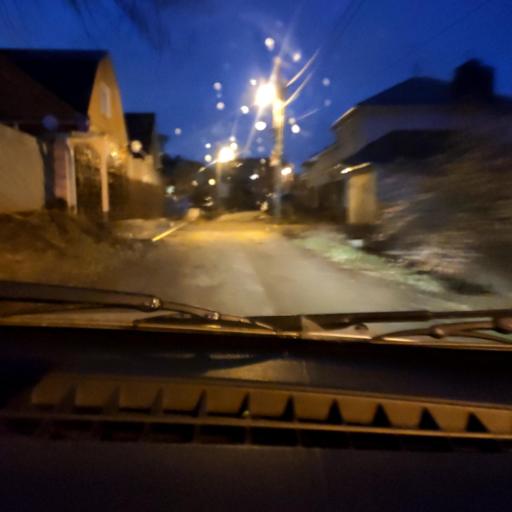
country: RU
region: Voronezj
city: Voronezh
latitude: 51.6306
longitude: 39.1817
